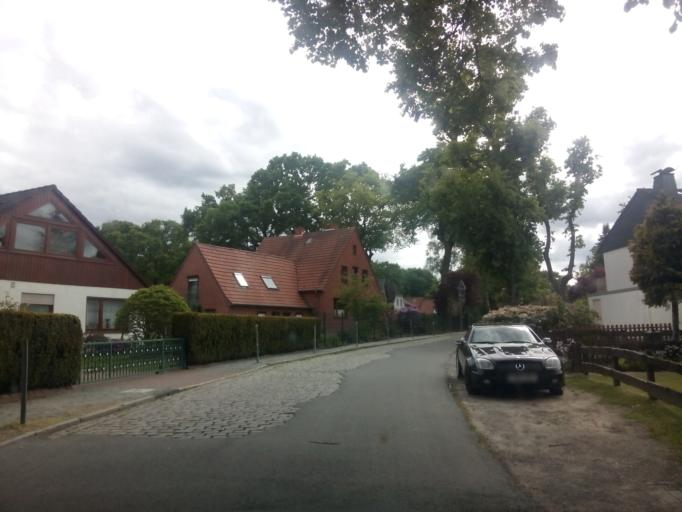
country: DE
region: Lower Saxony
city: Ritterhude
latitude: 53.1566
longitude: 8.7216
